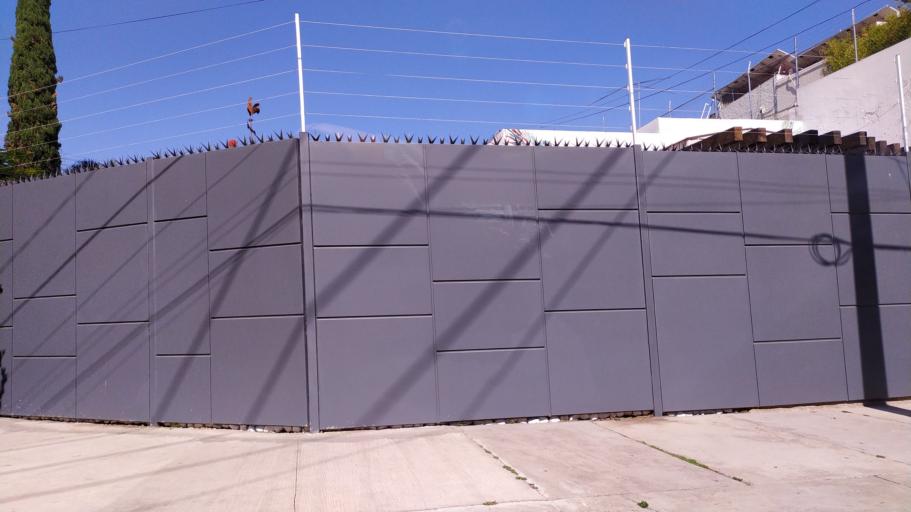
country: MX
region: Jalisco
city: Guadalajara
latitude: 20.6828
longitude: -103.3916
